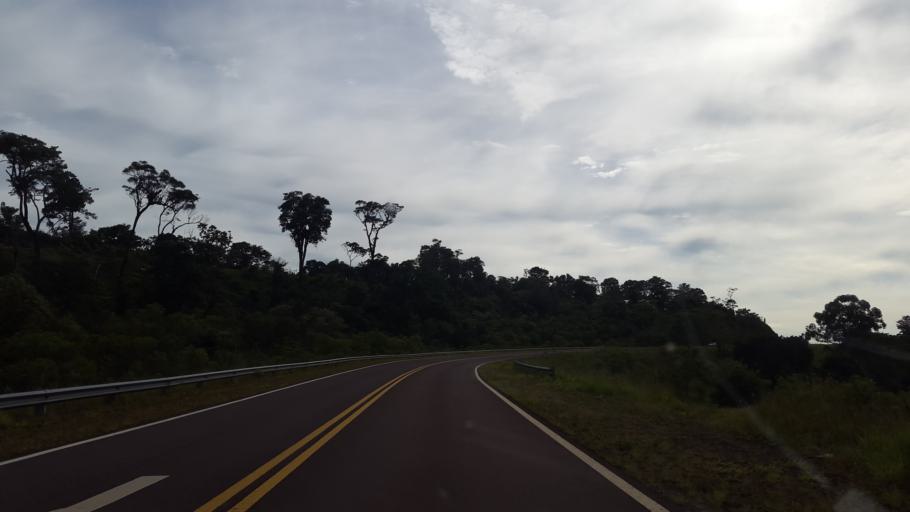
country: AR
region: Misiones
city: Bernardo de Irigoyen
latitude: -26.3846
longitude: -53.7963
